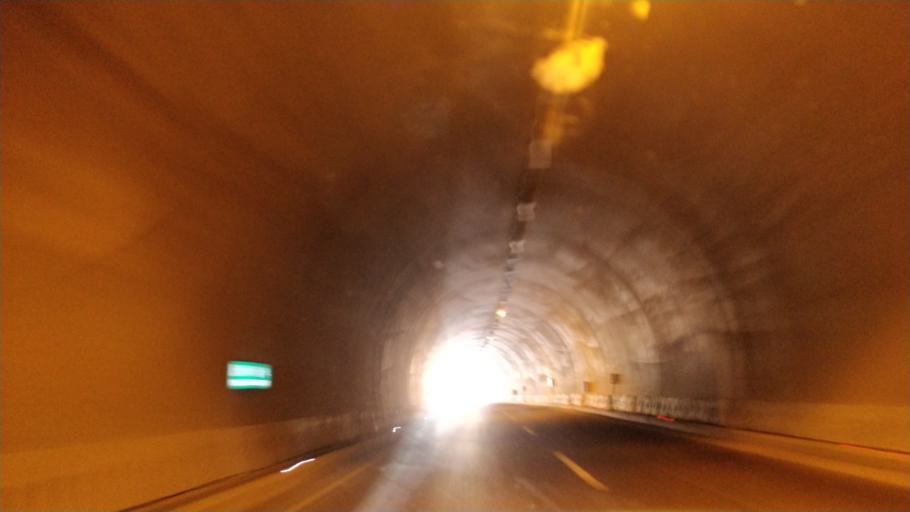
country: TR
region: Mersin
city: Ovacik
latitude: 36.1725
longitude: 33.5872
